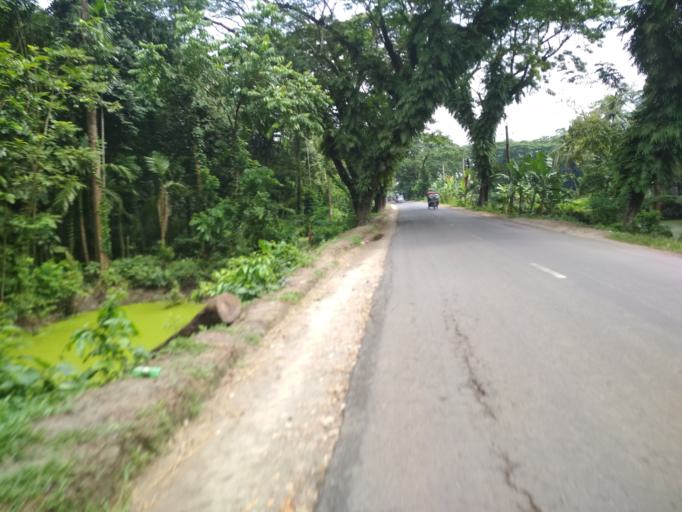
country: BD
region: Chittagong
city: Lakshmipur
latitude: 22.9633
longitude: 90.8097
